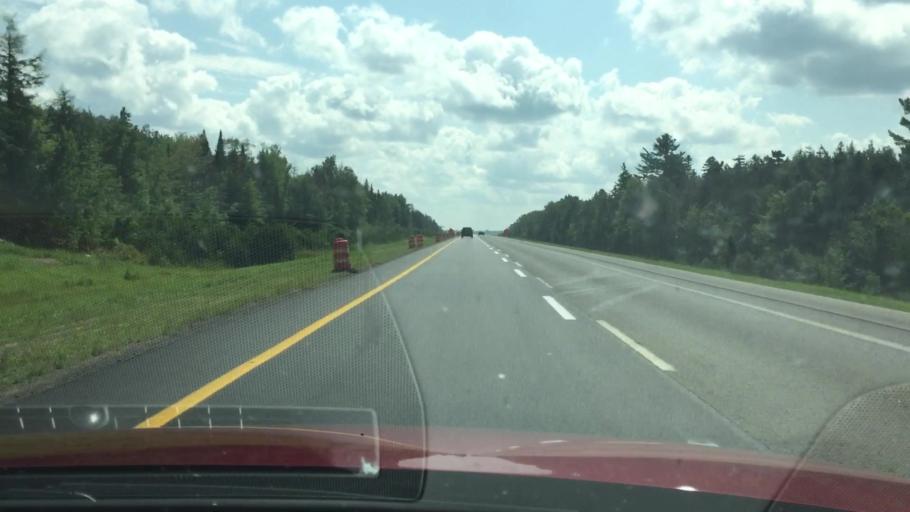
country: US
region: Maine
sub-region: Penobscot County
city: Medway
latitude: 45.6622
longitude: -68.4995
